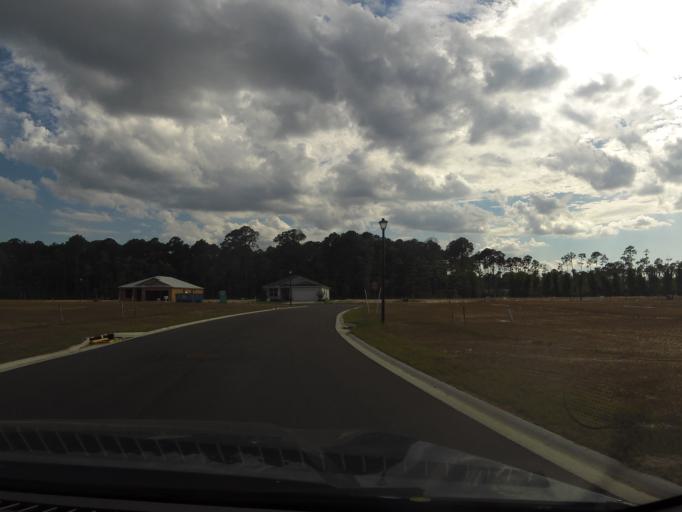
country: US
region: Florida
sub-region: Saint Johns County
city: Palm Valley
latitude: 30.1761
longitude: -81.5104
